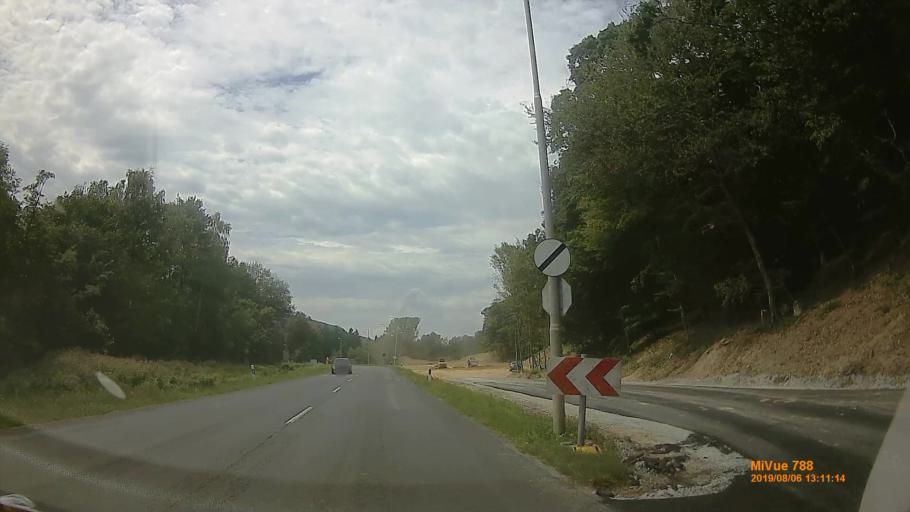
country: AT
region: Burgenland
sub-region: Politischer Bezirk Oberpullendorf
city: Mannersdorf an der Rabnitz
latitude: 47.4071
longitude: 16.5221
